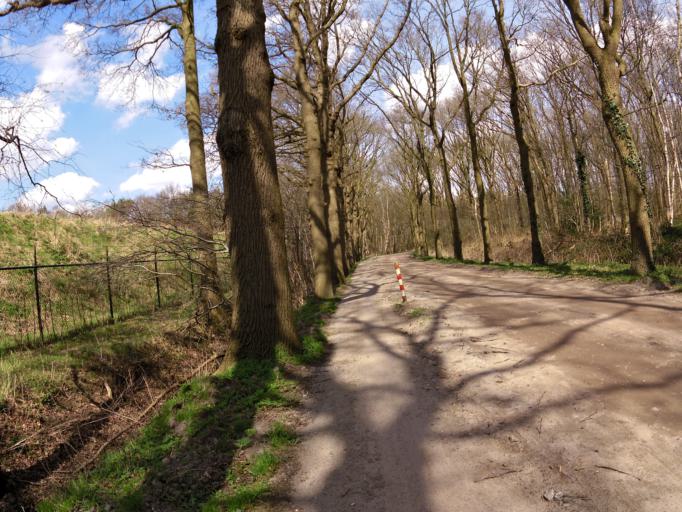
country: NL
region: North Brabant
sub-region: Gemeente Vught
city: Vught
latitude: 51.6454
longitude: 5.2576
